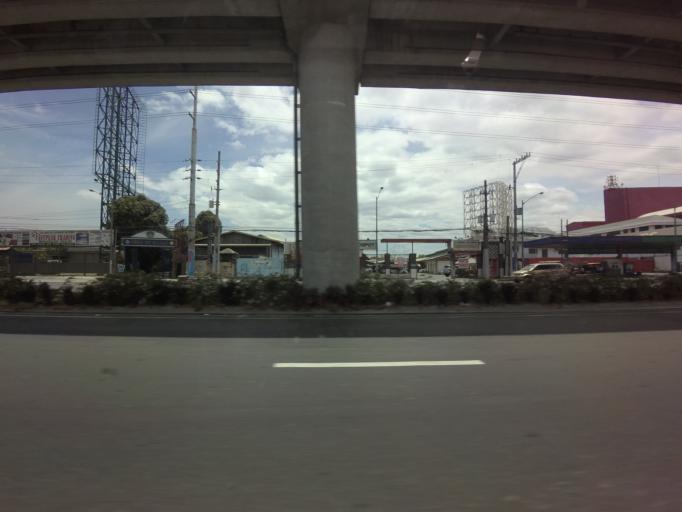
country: PH
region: Metro Manila
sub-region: Marikina
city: Calumpang
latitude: 14.6214
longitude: 121.1056
